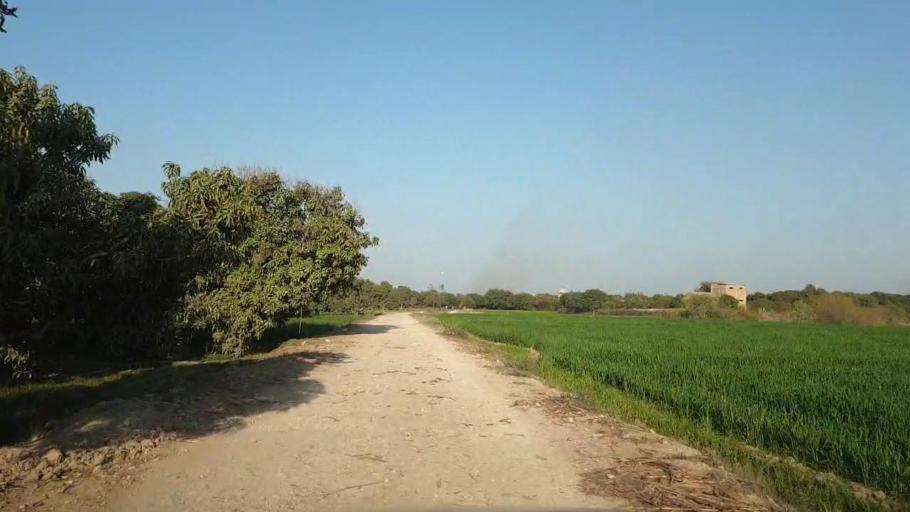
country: PK
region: Sindh
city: Tando Allahyar
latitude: 25.5037
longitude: 68.6393
